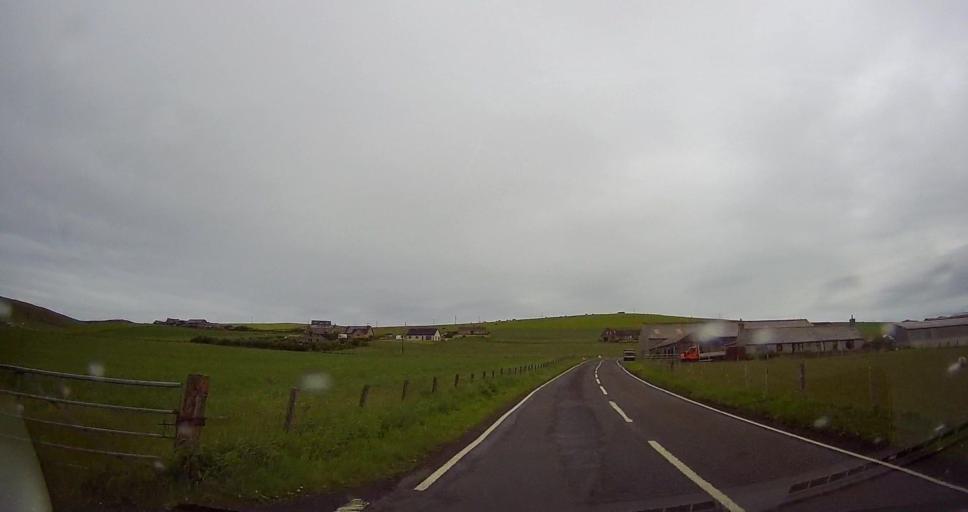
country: GB
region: Scotland
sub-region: Orkney Islands
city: Stromness
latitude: 58.9942
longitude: -3.2919
